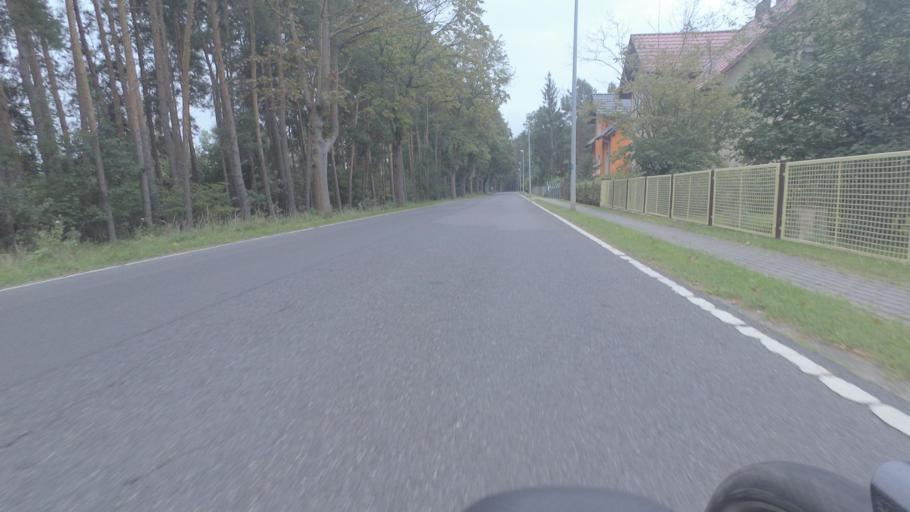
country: DE
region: Brandenburg
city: Luckenwalde
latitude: 52.1223
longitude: 13.1895
